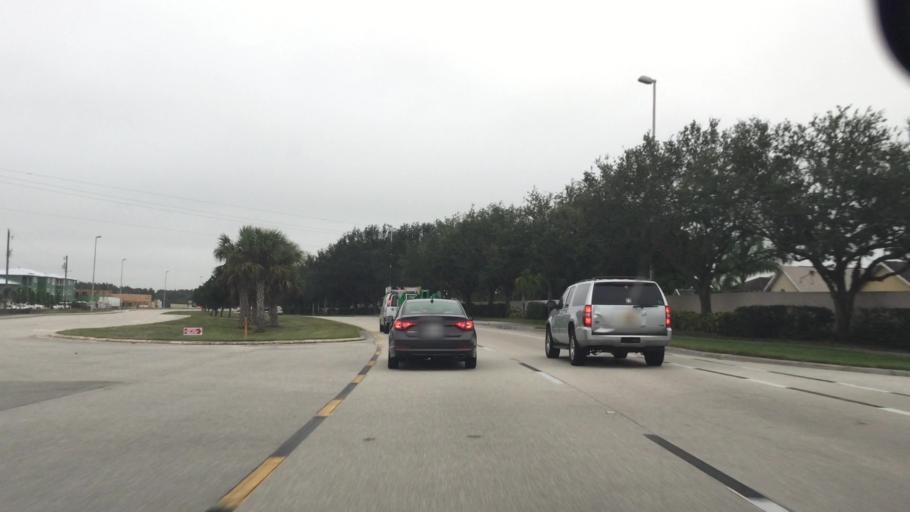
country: US
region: Florida
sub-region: Lee County
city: Three Oaks
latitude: 26.4816
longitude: -81.7980
